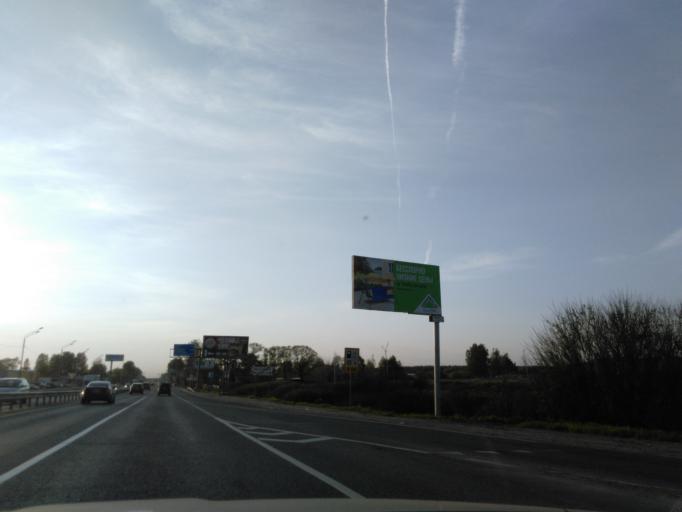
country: RU
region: Moskovskaya
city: Novopodrezkovo
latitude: 55.9567
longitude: 37.3415
